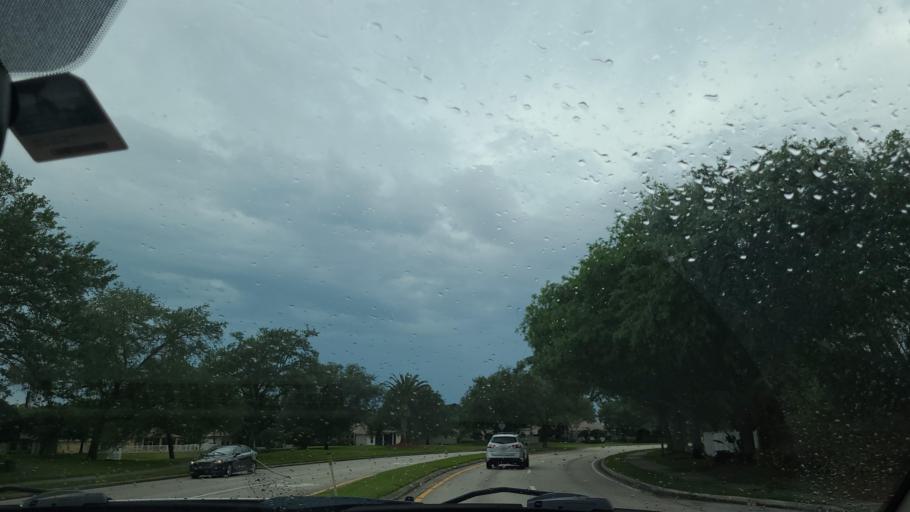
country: US
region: Florida
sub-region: Brevard County
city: Grant-Valkaria
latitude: 27.9557
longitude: -80.6488
